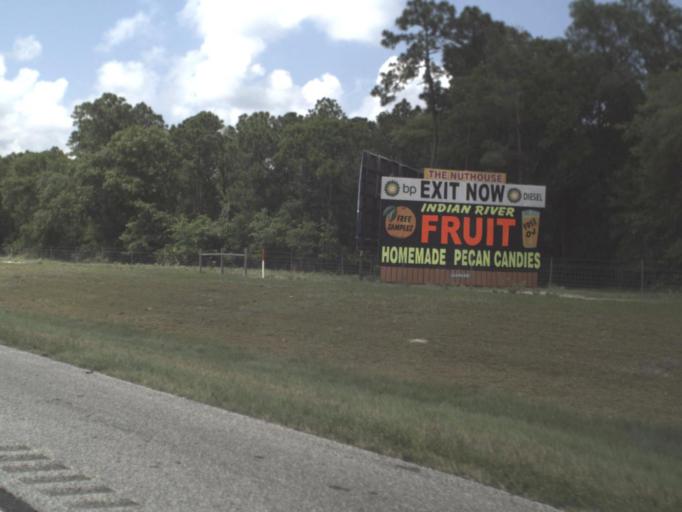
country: US
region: Florida
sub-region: Flagler County
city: Palm Coast
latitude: 29.6560
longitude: -81.2787
